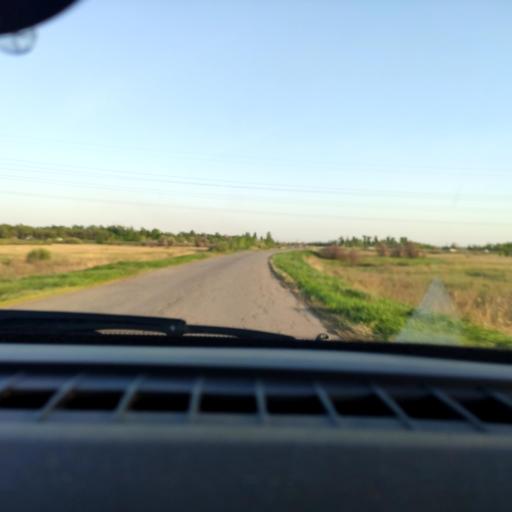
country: RU
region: Samara
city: Georgiyevka
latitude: 53.2667
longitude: 50.9611
